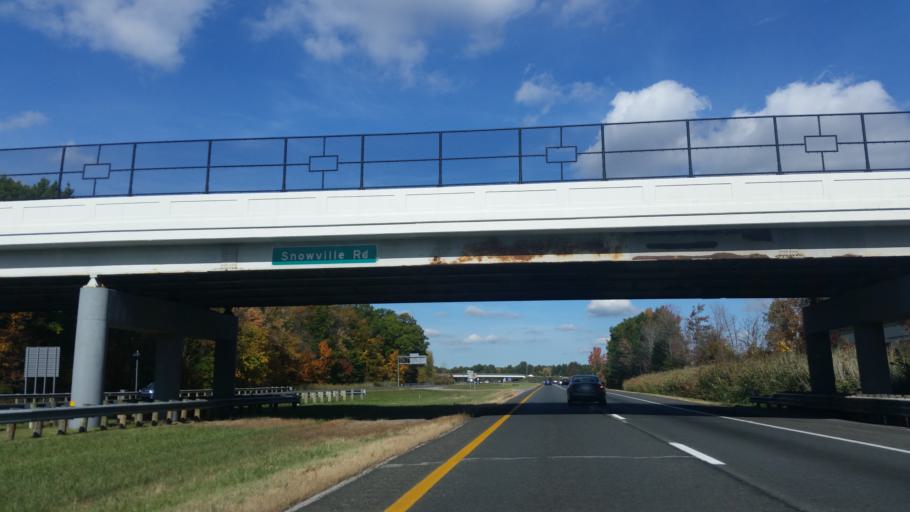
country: US
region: Ohio
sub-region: Cuyahoga County
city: Brecksville
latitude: 41.2827
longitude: -81.6361
